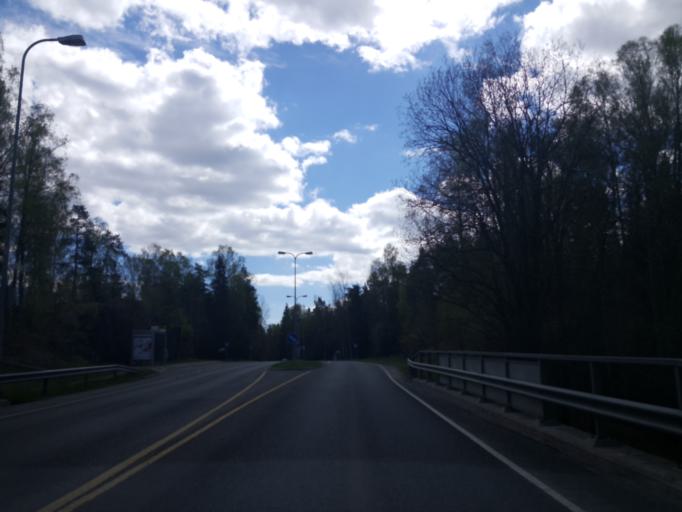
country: FI
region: Uusimaa
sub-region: Helsinki
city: Kilo
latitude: 60.2779
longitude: 24.8360
